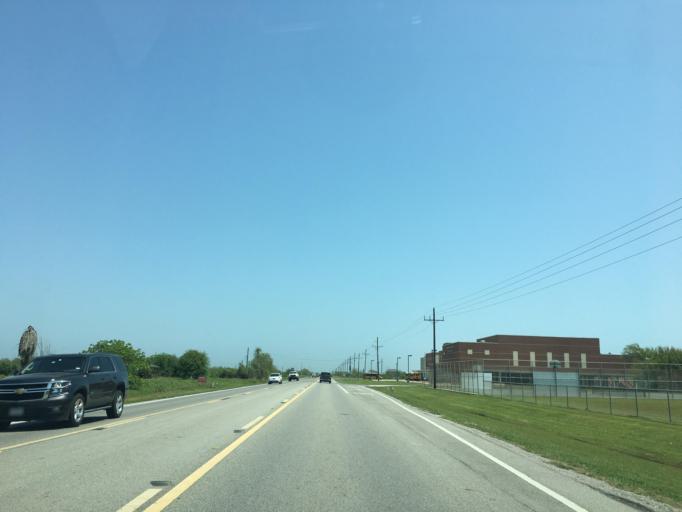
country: US
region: Texas
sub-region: Galveston County
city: Bolivar Peninsula
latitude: 29.4271
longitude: -94.6922
